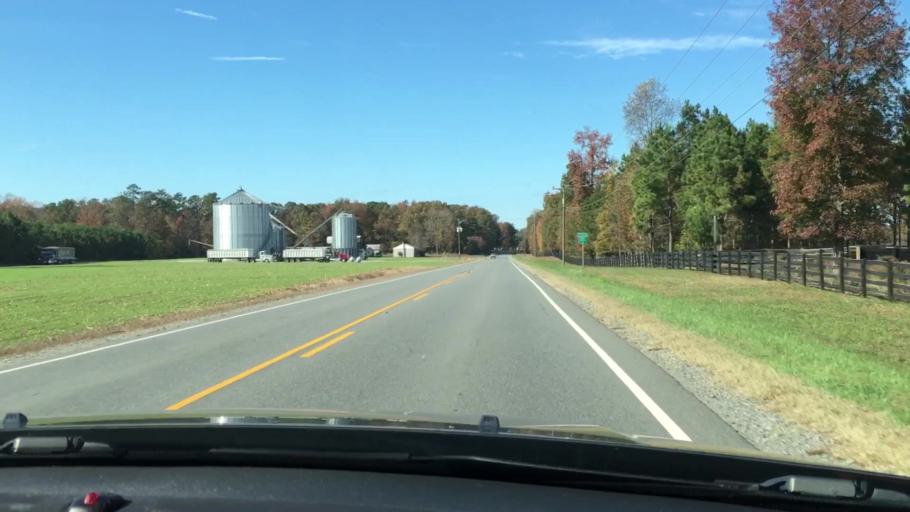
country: US
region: Virginia
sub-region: King and Queen County
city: King and Queen Court House
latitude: 37.5940
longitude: -76.9006
